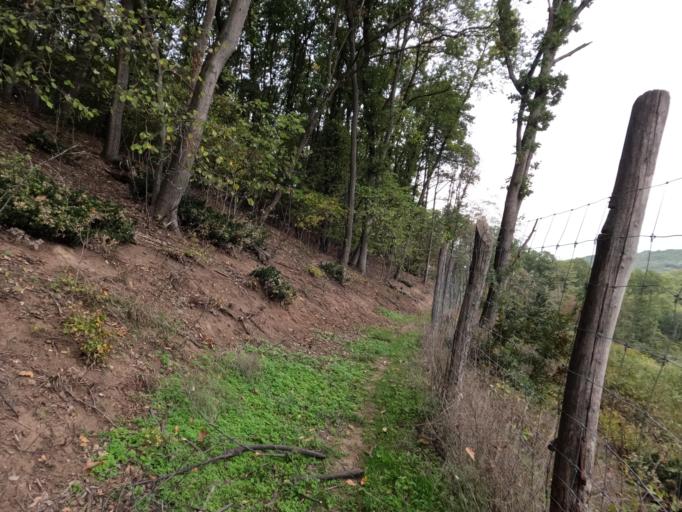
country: HU
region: Tolna
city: Szentgalpuszta
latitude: 46.3248
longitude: 18.6163
